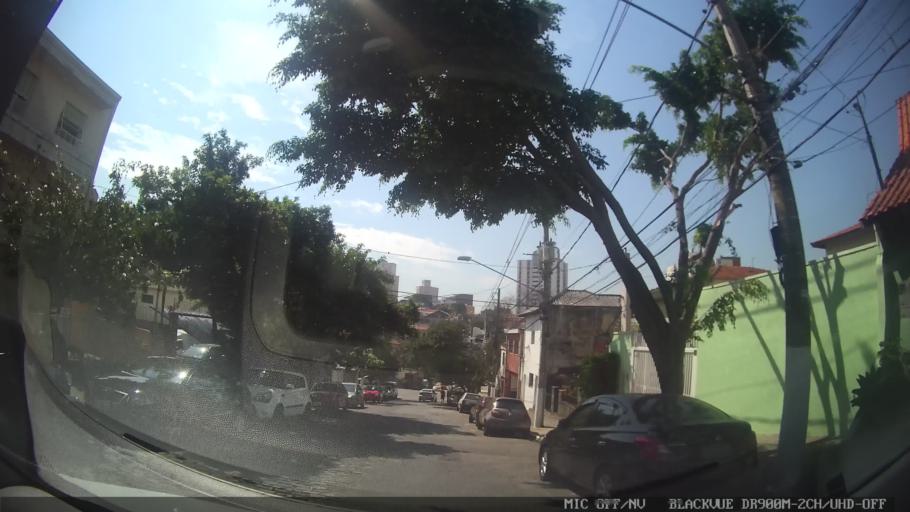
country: BR
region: Sao Paulo
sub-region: Sao Paulo
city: Sao Paulo
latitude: -23.5798
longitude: -46.6161
